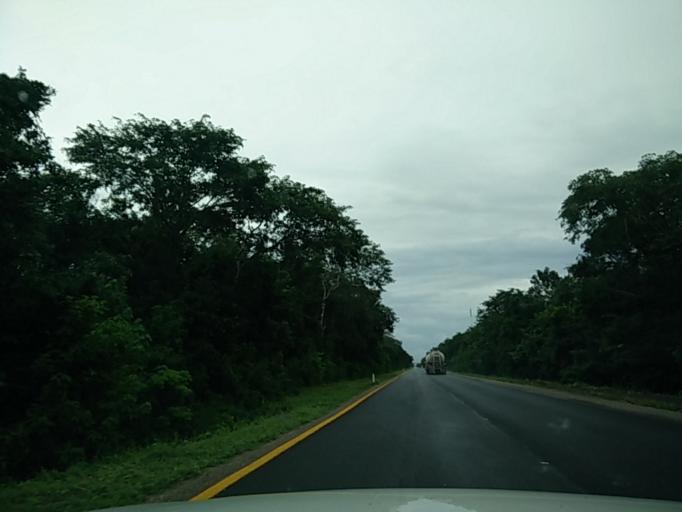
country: MX
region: Quintana Roo
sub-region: Lazaro Cardenas
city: Ignacio Zaragoza
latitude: 20.8867
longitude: -87.5538
